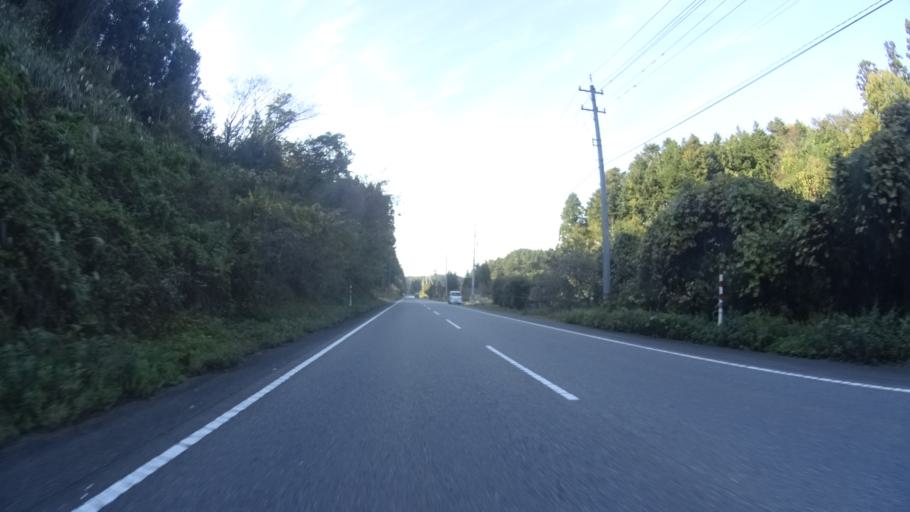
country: JP
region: Ishikawa
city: Hakui
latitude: 37.0122
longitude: 136.7979
